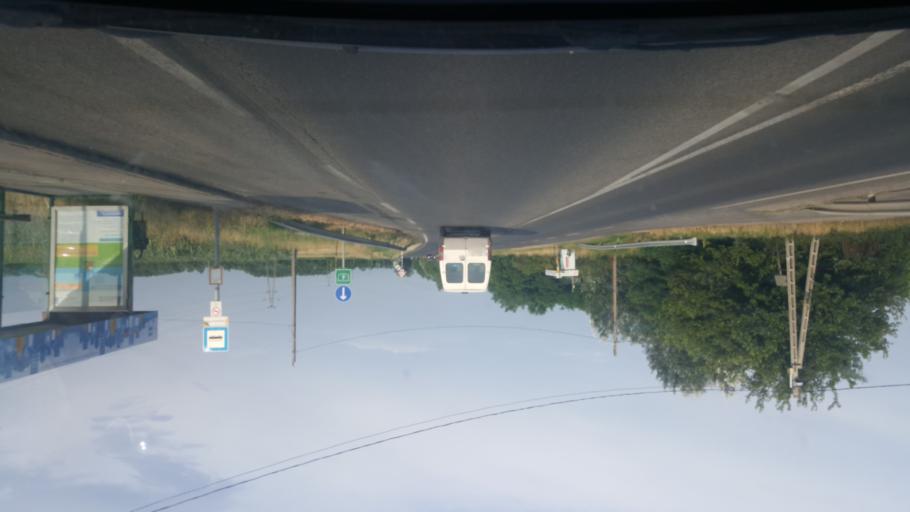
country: HU
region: Pest
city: Peteri
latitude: 47.3640
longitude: 19.3846
